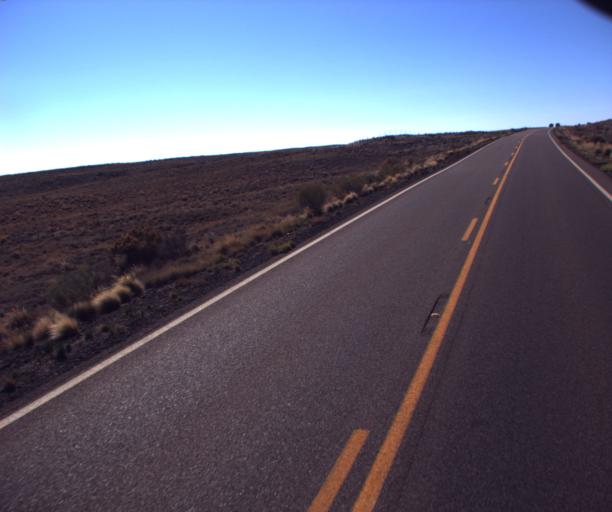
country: US
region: Arizona
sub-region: Navajo County
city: Dilkon
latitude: 35.2408
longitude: -110.4304
